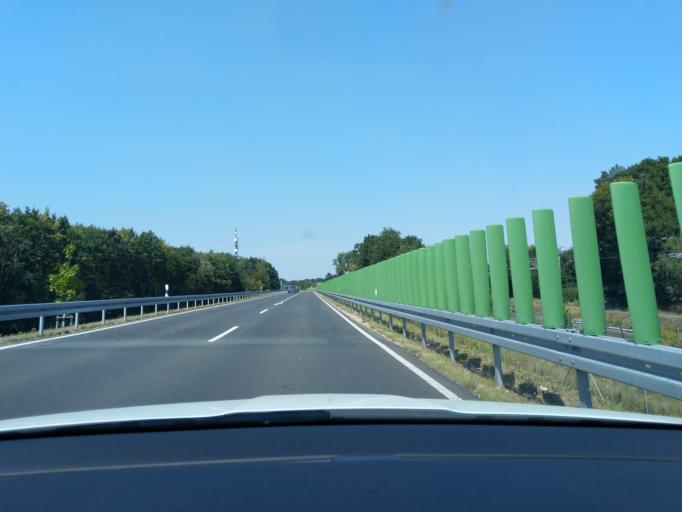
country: DE
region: North Rhine-Westphalia
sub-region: Regierungsbezirk Koln
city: Wassenberg
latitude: 51.1168
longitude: 6.2028
